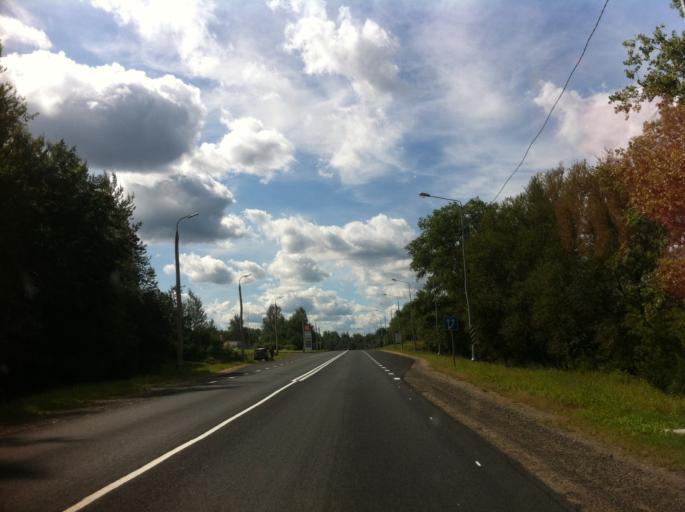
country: RU
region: Pskov
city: Izborsk
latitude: 57.7097
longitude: 27.8924
